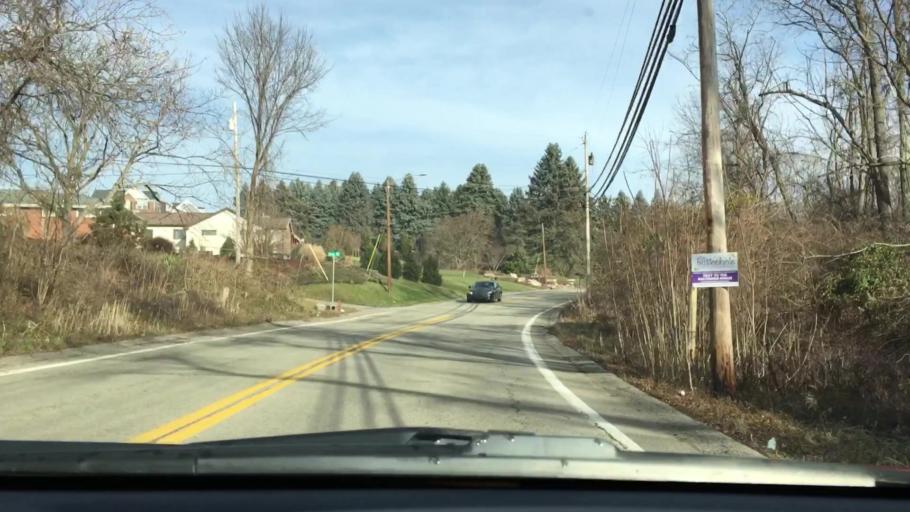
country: US
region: Pennsylvania
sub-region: Allegheny County
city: South Park Township
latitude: 40.2946
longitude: -79.9633
